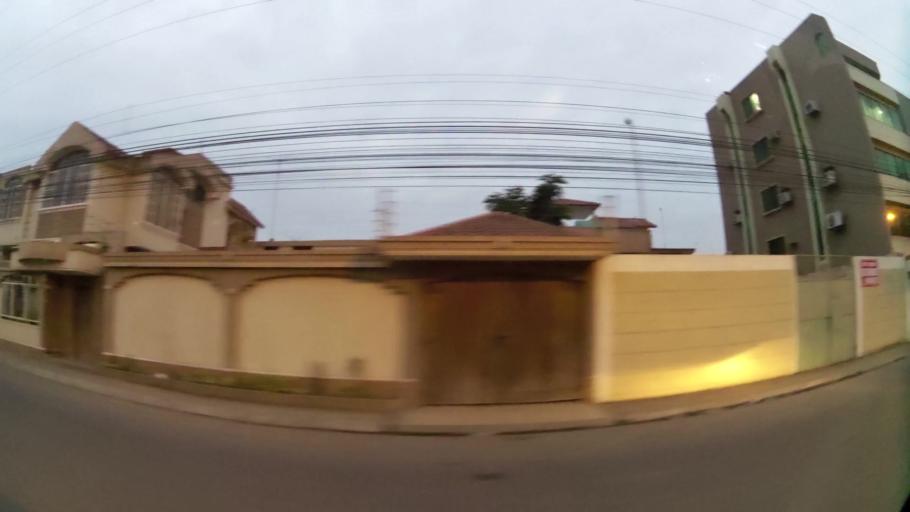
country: EC
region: El Oro
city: Machala
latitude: -3.2627
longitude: -79.9393
